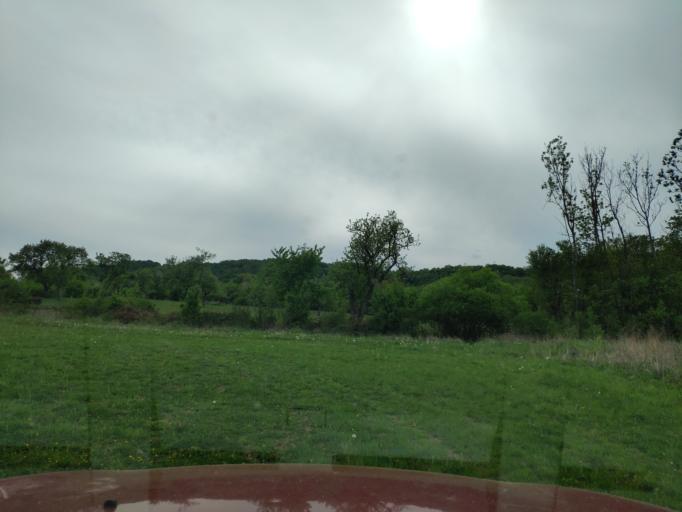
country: SK
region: Banskobystricky
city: Revuca
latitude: 48.5201
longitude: 20.1312
